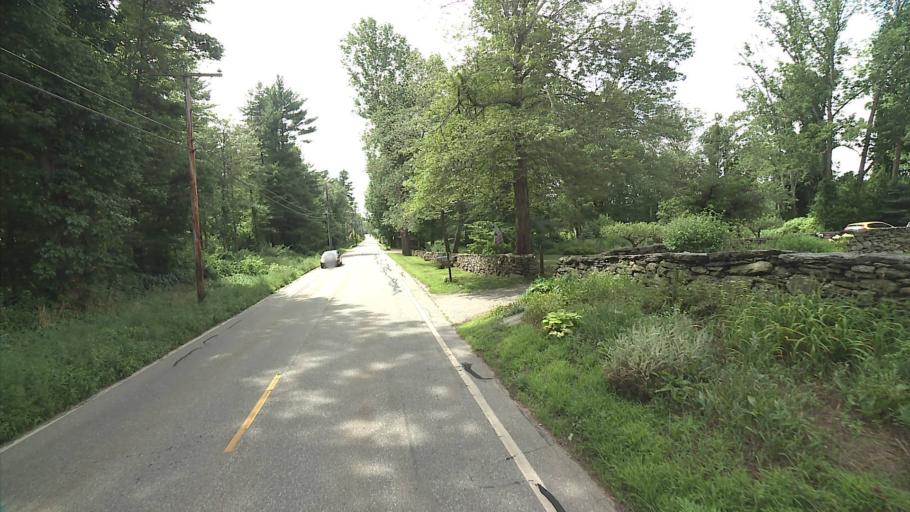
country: US
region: Connecticut
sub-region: Windham County
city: Thompson
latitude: 41.9357
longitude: -71.8665
